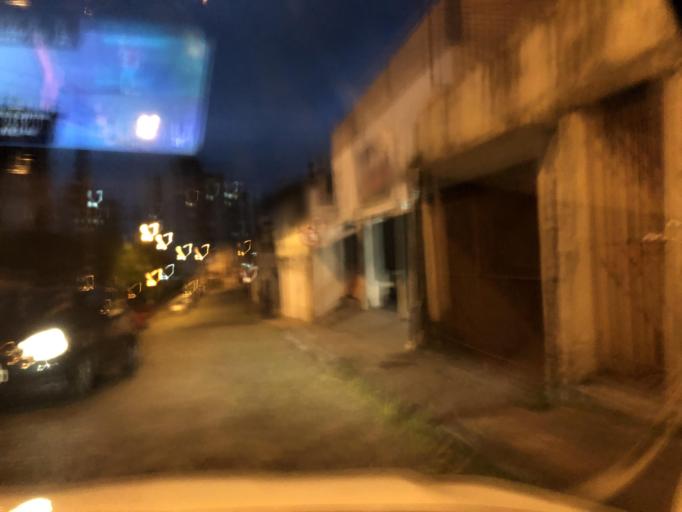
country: BR
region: Santa Catarina
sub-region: Florianopolis
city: Morro da Cruz
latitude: -27.5858
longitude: -48.5422
